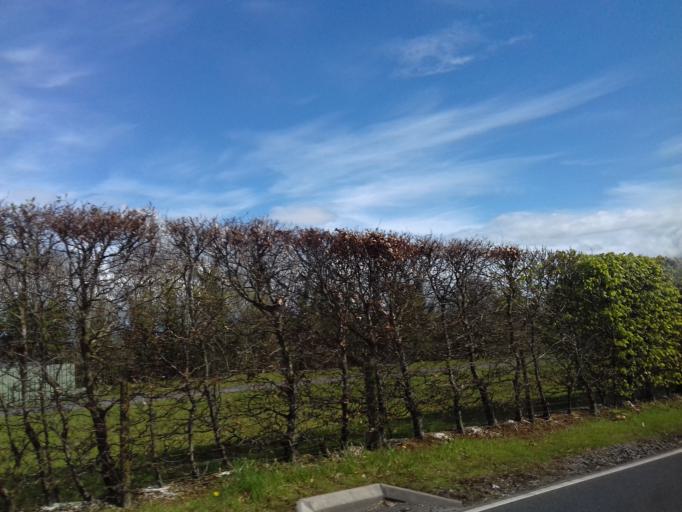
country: GB
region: Northern Ireland
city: Irvinestown
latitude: 54.4469
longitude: -7.7942
